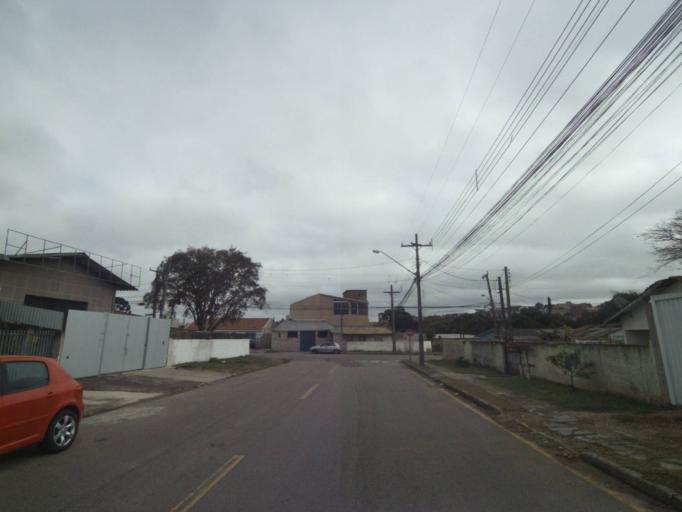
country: BR
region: Parana
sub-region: Curitiba
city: Curitiba
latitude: -25.5047
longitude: -49.2844
